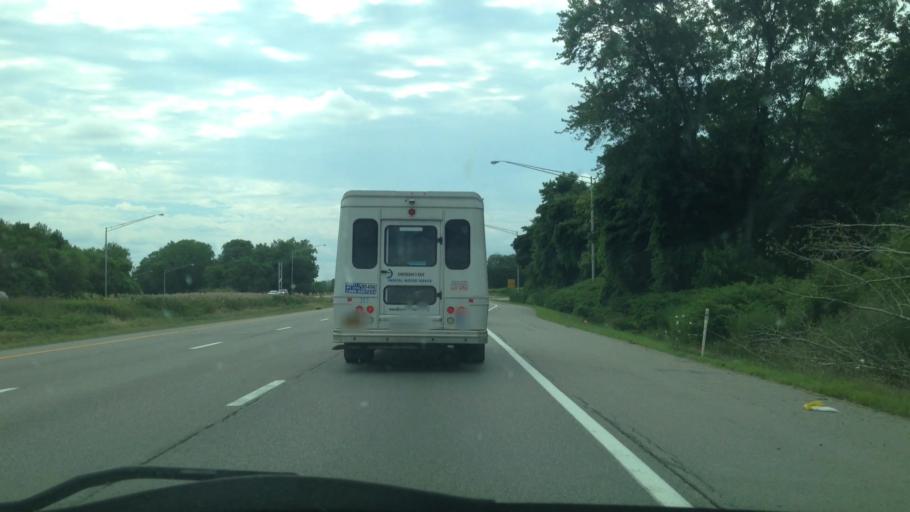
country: US
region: New York
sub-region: Monroe County
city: North Gates
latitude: 43.1432
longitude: -77.6727
